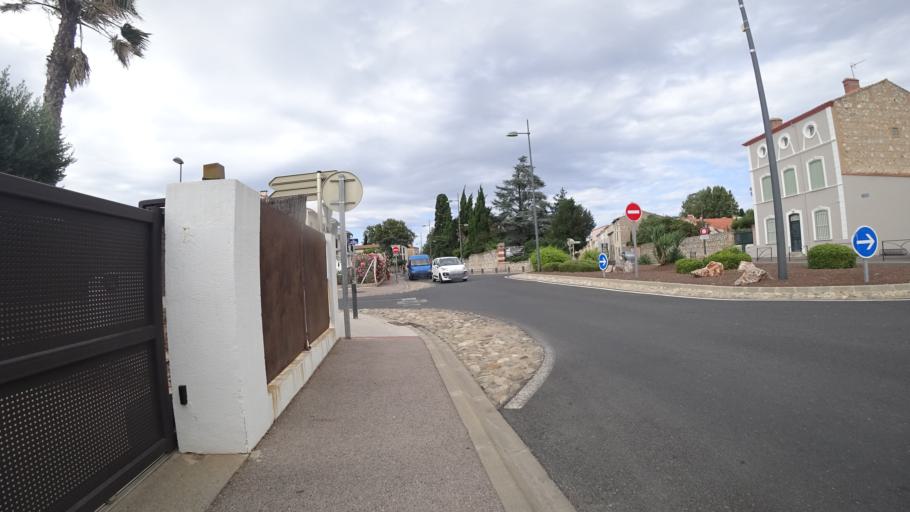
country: FR
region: Languedoc-Roussillon
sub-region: Departement des Pyrenees-Orientales
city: Saint-Laurent-de-la-Salanque
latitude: 42.7702
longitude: 2.9870
